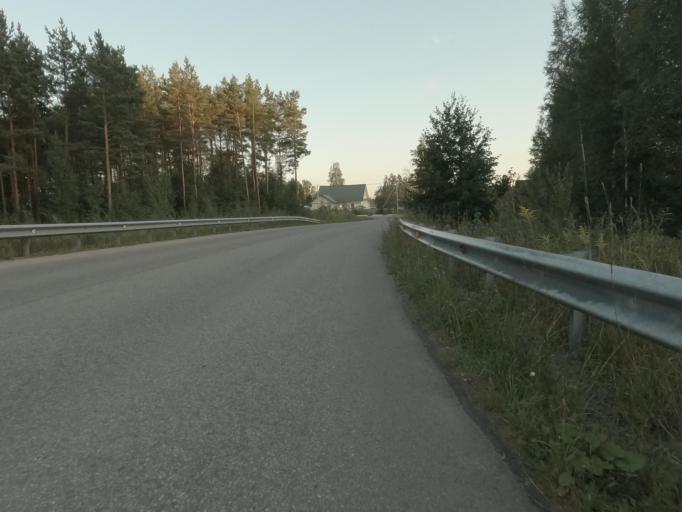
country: RU
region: Leningrad
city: Mga
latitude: 59.7614
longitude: 31.0404
